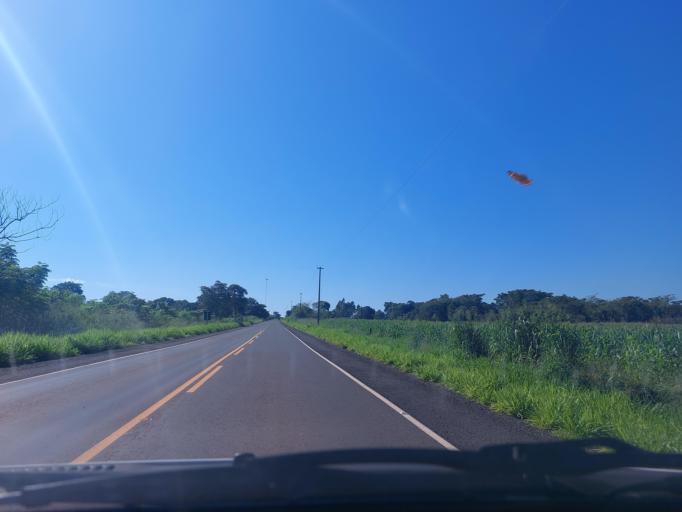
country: PY
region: San Pedro
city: Guayaybi
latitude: -24.3176
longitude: -56.1784
